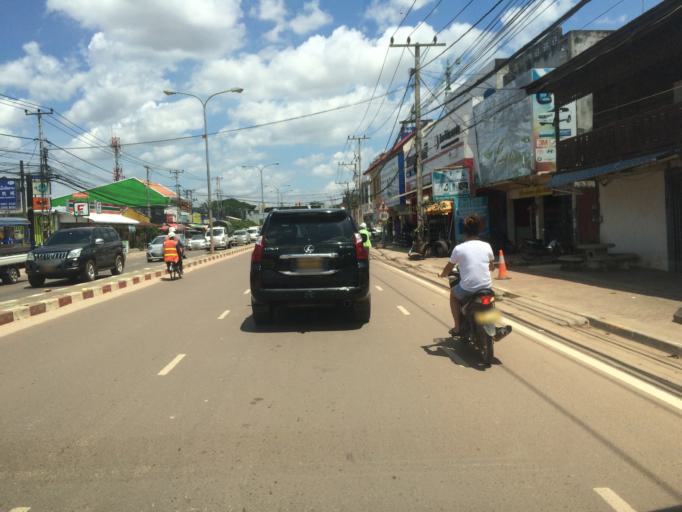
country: TH
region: Nong Khai
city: Si Chiang Mai
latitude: 17.9722
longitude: 102.5654
